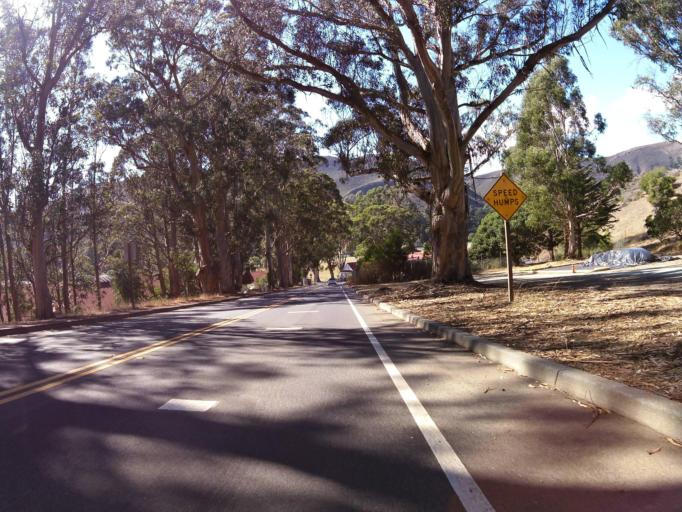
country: US
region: California
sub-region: Marin County
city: Sausalito
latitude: 37.8360
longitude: -122.4750
